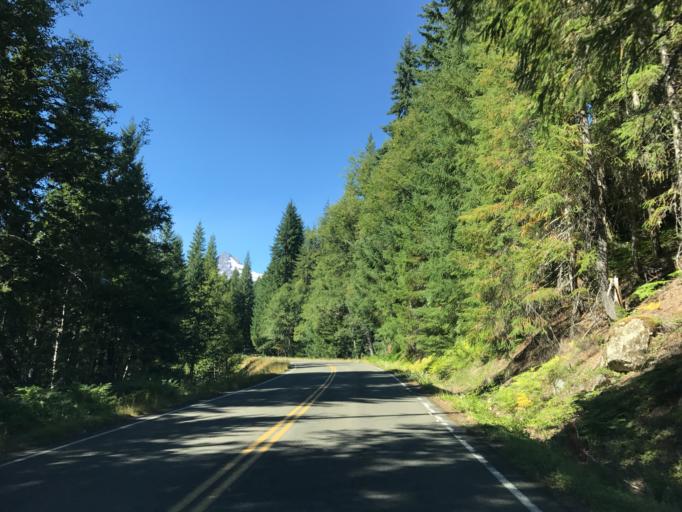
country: US
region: Washington
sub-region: Pierce County
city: Buckley
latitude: 46.7624
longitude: -121.6307
